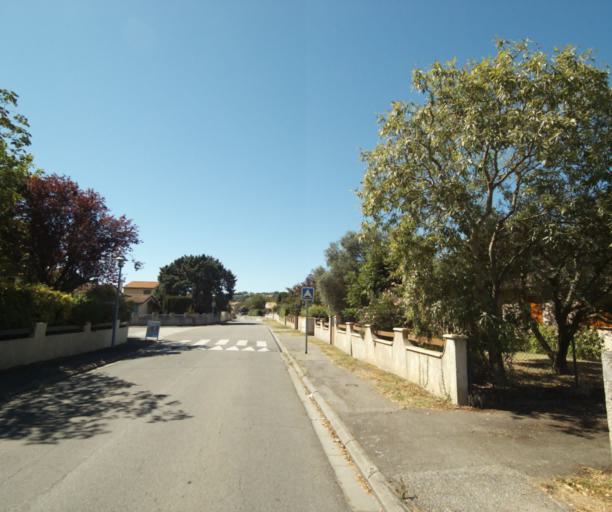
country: FR
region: Midi-Pyrenees
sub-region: Departement de la Haute-Garonne
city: Pechabou
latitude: 43.5095
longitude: 1.5147
